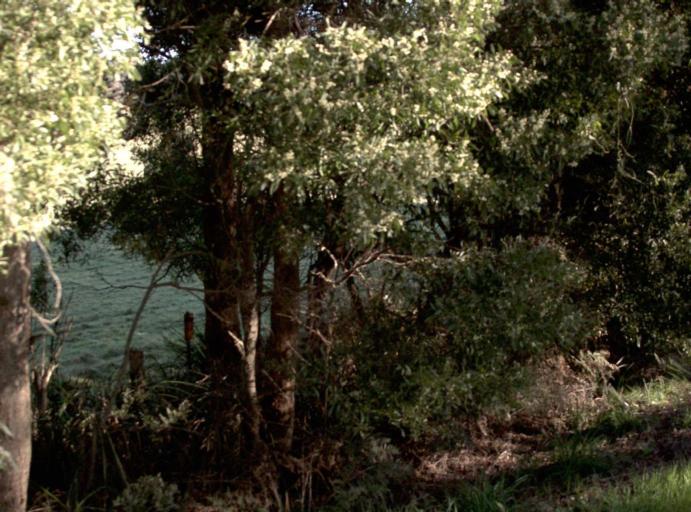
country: AU
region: Tasmania
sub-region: Dorset
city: Bridport
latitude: -41.1043
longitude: 147.1980
